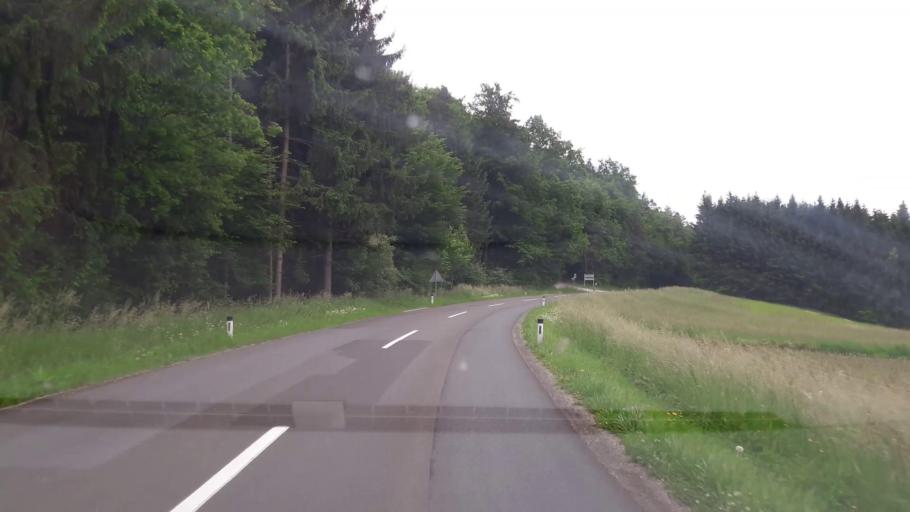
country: AT
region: Styria
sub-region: Politischer Bezirk Hartberg-Fuerstenfeld
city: Soechau
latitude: 47.0564
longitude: 16.0107
